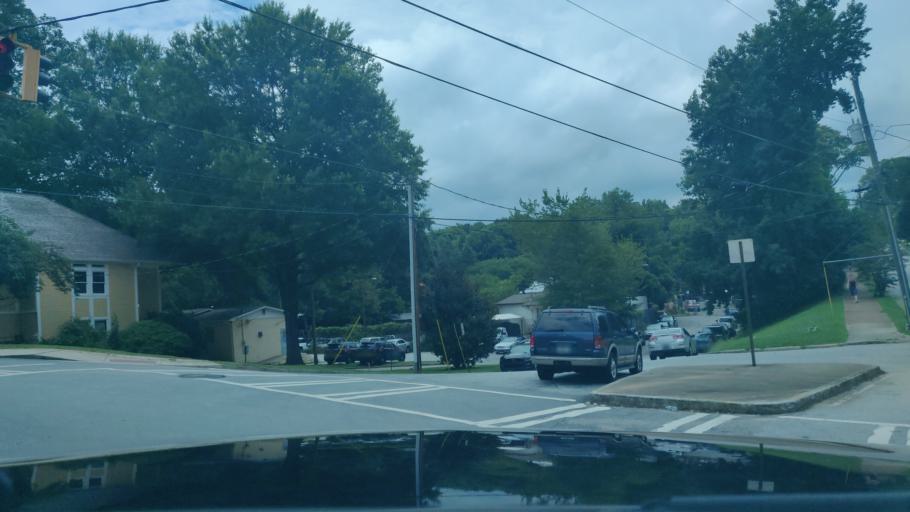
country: US
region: Georgia
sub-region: Fulton County
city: Atlanta
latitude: 33.7303
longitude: -84.3737
